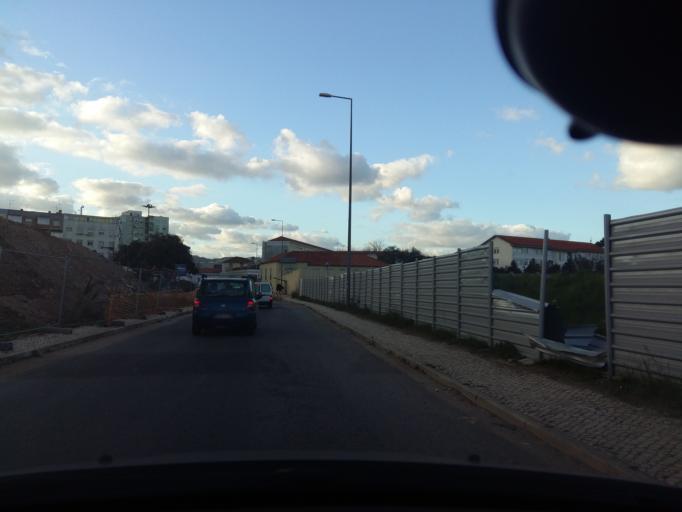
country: PT
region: Lisbon
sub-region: Odivelas
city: Pontinha
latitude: 38.7634
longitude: -9.1960
